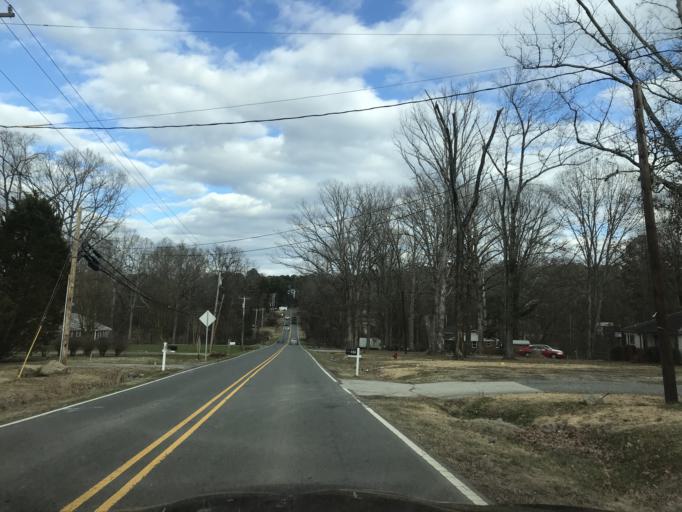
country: US
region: North Carolina
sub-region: Durham County
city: Durham
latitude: 35.9662
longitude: -78.8443
